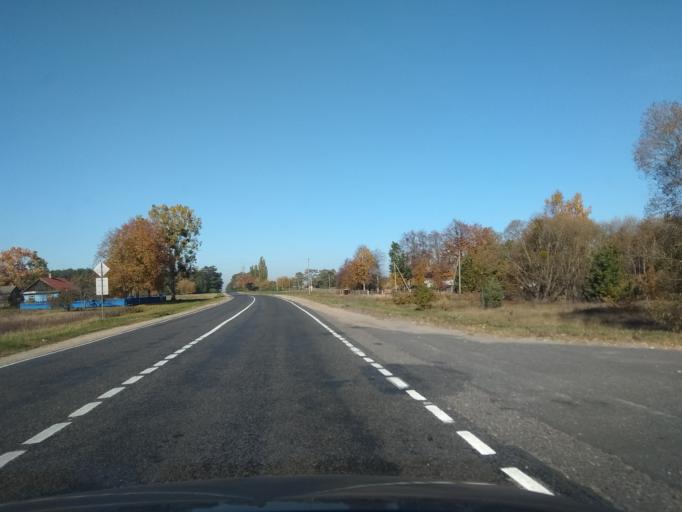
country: BY
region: Brest
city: Malaryta
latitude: 51.9268
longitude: 24.0704
